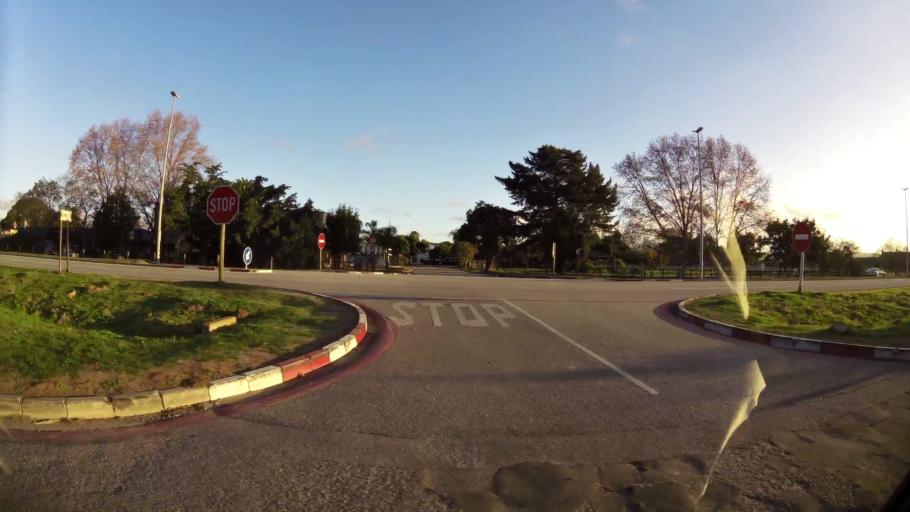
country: ZA
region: Western Cape
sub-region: Eden District Municipality
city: Knysna
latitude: -34.0132
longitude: 22.8003
